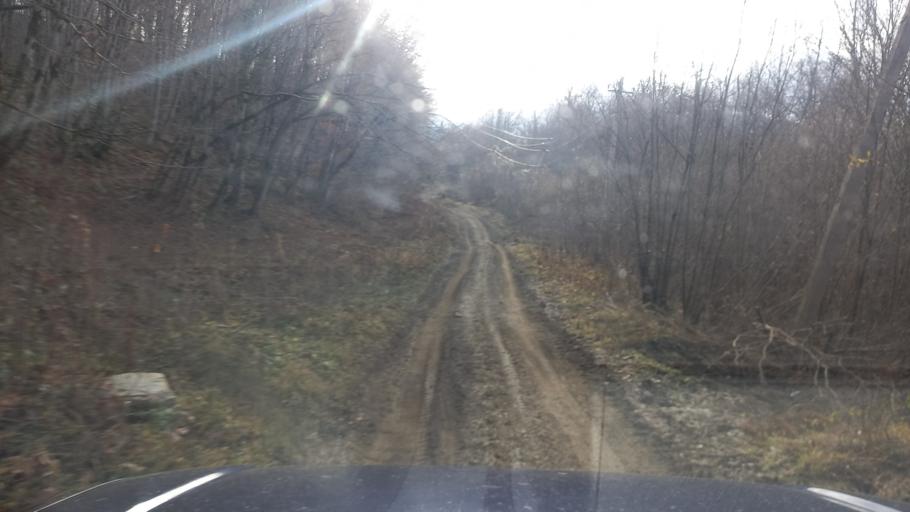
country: RU
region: Krasnodarskiy
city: Neftegorsk
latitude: 44.2050
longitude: 39.7058
